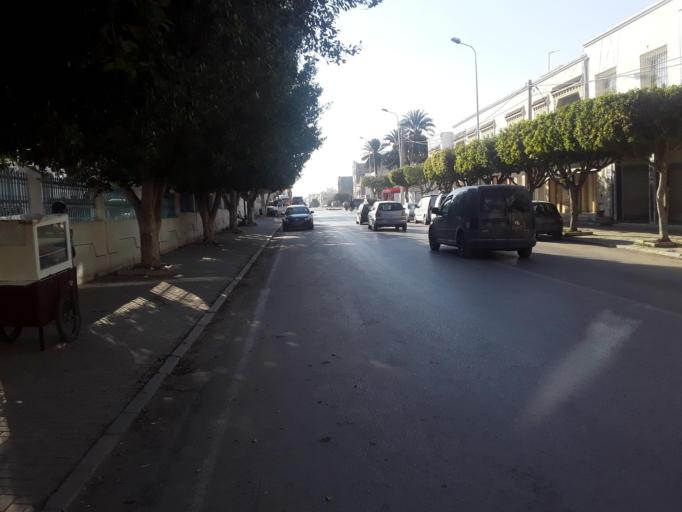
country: TN
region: Al Qayrawan
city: Kairouan
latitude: 35.6814
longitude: 10.0995
